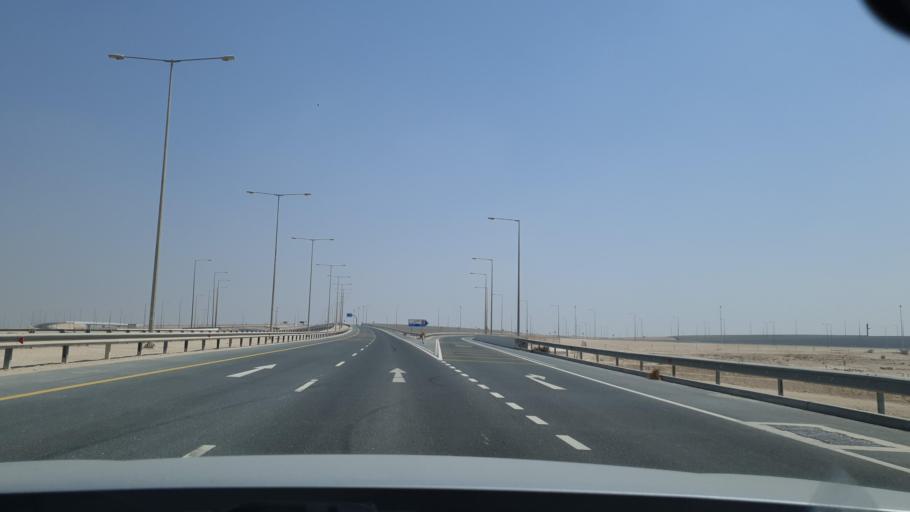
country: QA
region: Baladiyat az Za`ayin
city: Az Za`ayin
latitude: 25.6175
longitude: 51.3603
